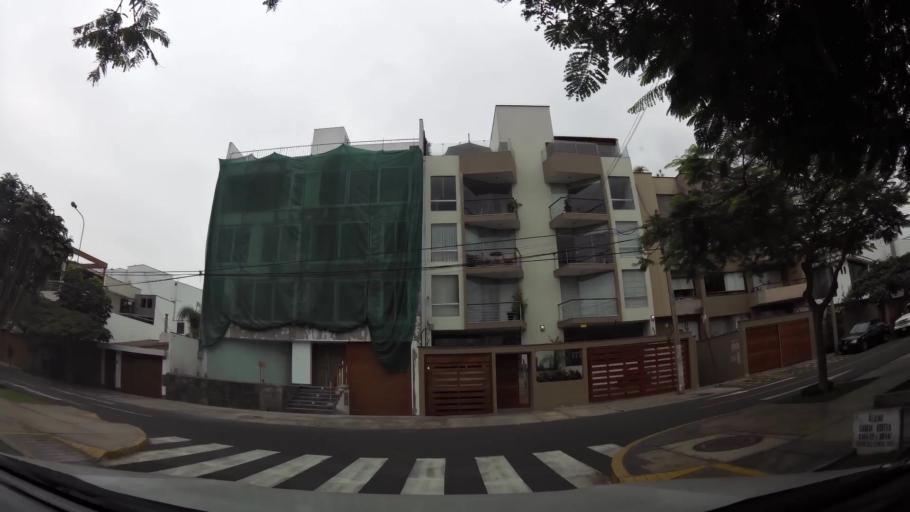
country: PE
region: Lima
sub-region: Lima
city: Surco
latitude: -12.1224
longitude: -77.0095
